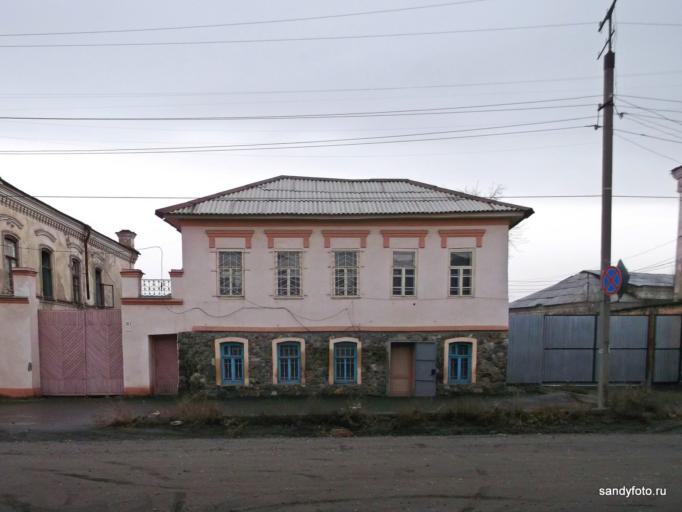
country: RU
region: Chelyabinsk
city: Troitsk
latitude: 54.0812
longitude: 61.5603
